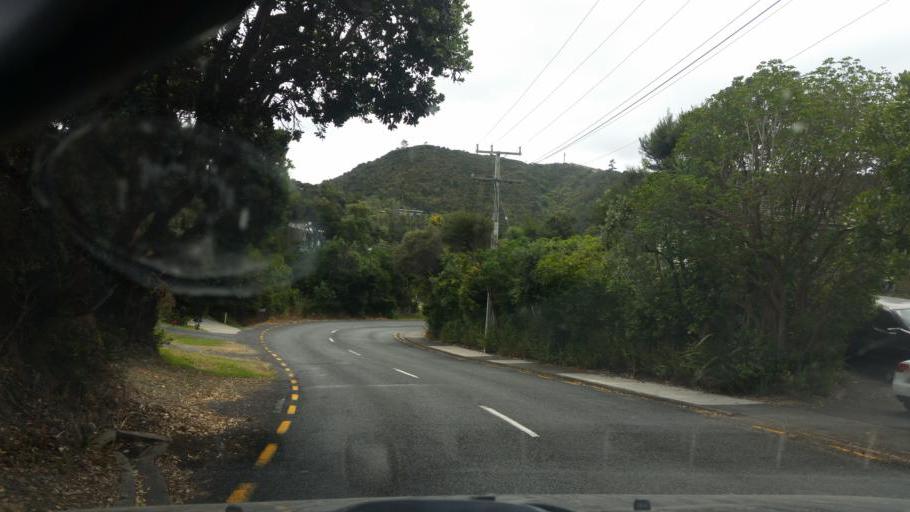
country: NZ
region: Auckland
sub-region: Auckland
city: Wellsford
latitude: -36.0829
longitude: 174.5892
